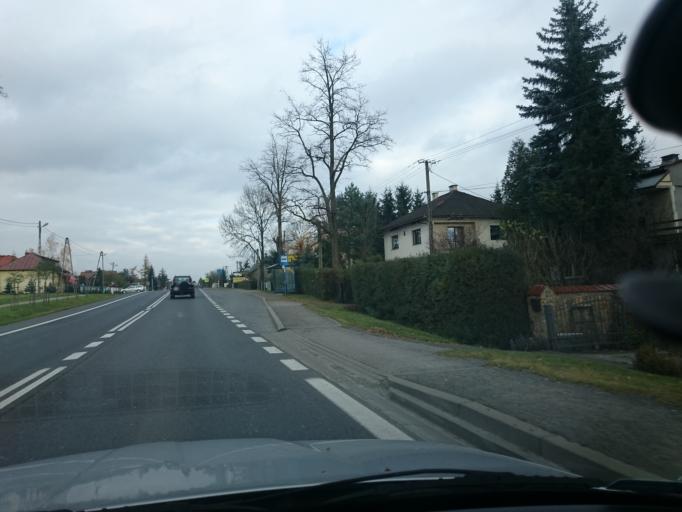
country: PL
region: Lesser Poland Voivodeship
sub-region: Powiat krakowski
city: Michalowice
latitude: 50.1610
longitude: 19.9798
